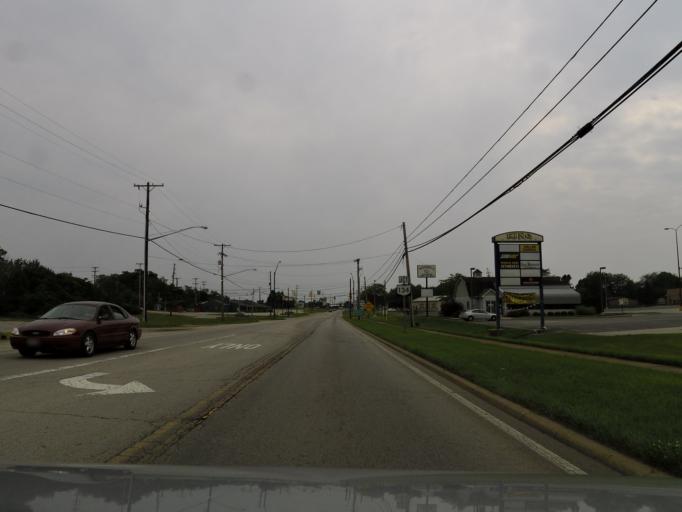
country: US
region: Ohio
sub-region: Clinton County
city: Wilmington
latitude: 39.4332
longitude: -83.8306
